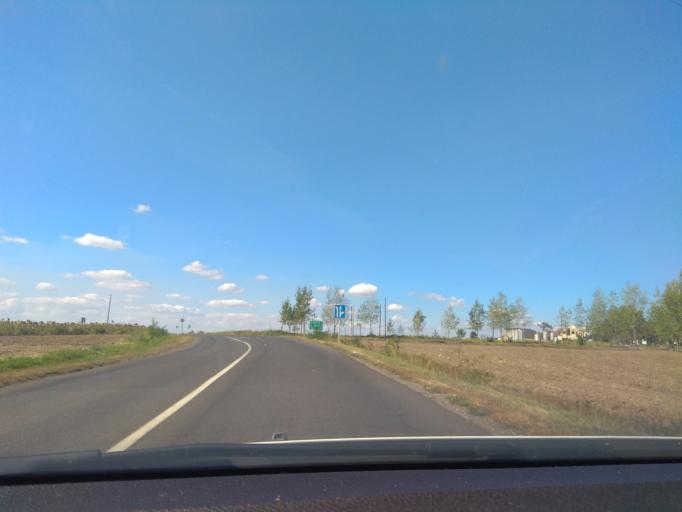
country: HU
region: Borsod-Abauj-Zemplen
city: Tallya
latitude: 48.2270
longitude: 21.2361
